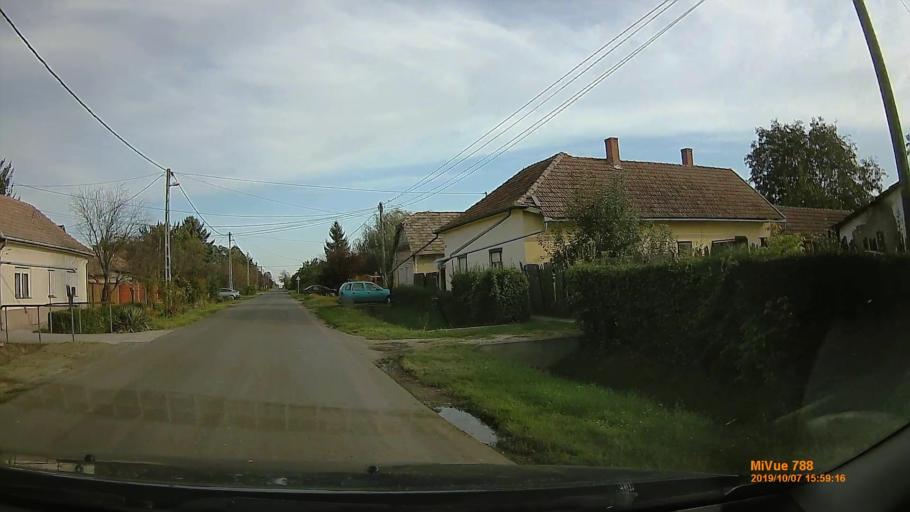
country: HU
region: Bekes
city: Szarvas
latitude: 46.8255
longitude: 20.6525
